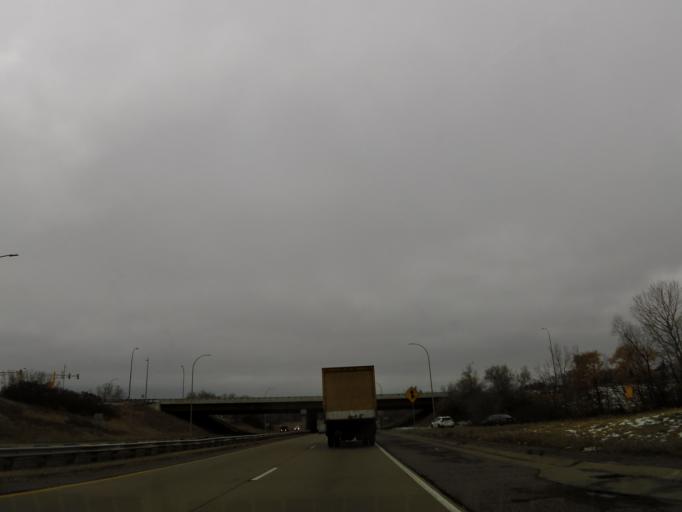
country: US
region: Minnesota
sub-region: Hennepin County
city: Minnetonka Mills
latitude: 44.9358
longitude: -93.3969
